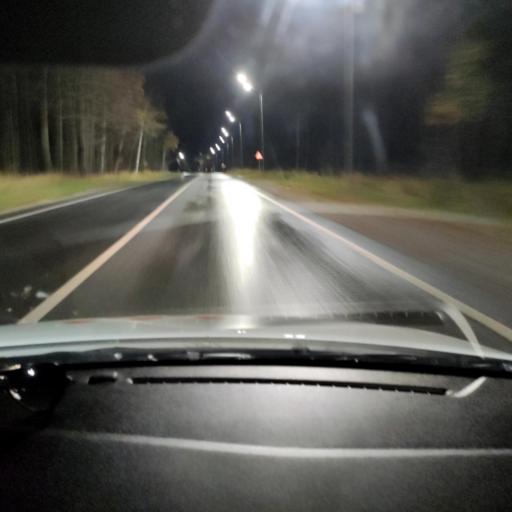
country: RU
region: Tatarstan
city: Stolbishchi
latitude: 55.6335
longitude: 49.0948
